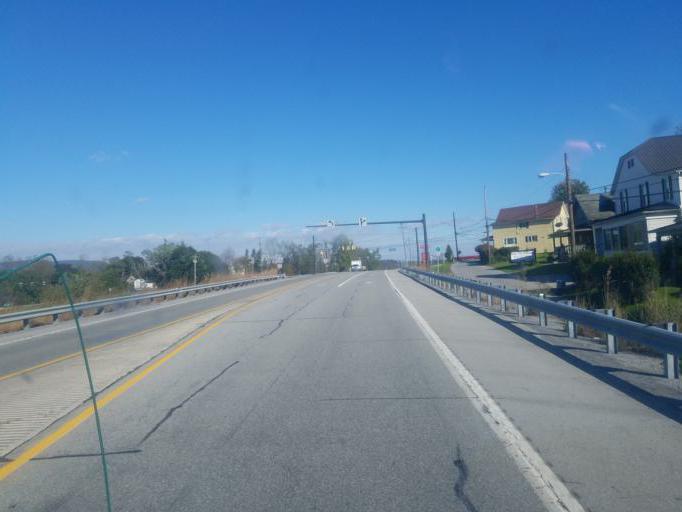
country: US
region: Pennsylvania
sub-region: Blair County
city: Claysburg
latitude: 40.2711
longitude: -78.4604
